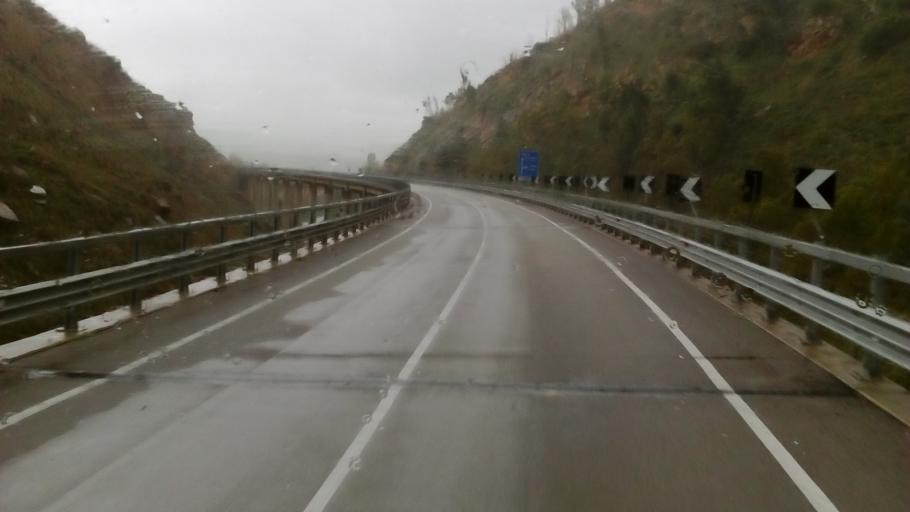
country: IT
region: Sicily
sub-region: Enna
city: Pietraperzia
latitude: 37.4999
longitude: 14.1412
